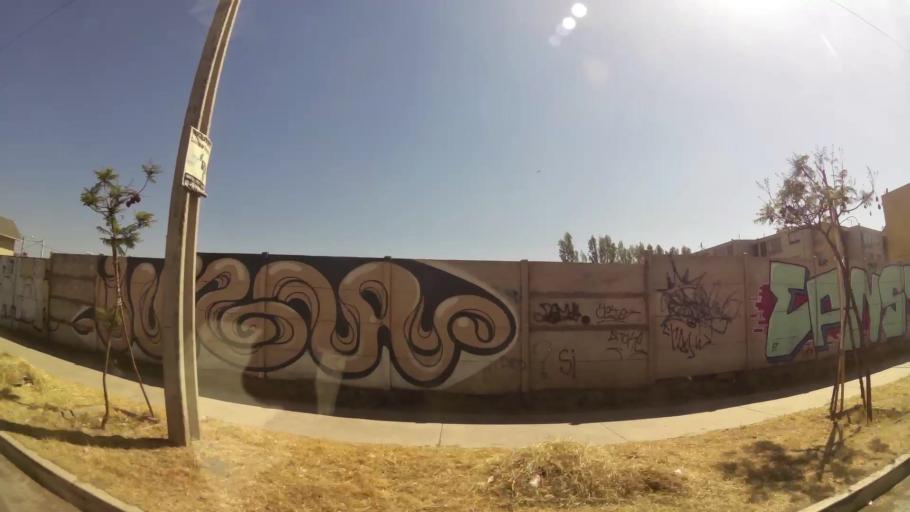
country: CL
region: Santiago Metropolitan
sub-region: Provincia de Maipo
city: San Bernardo
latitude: -33.6152
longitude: -70.6860
